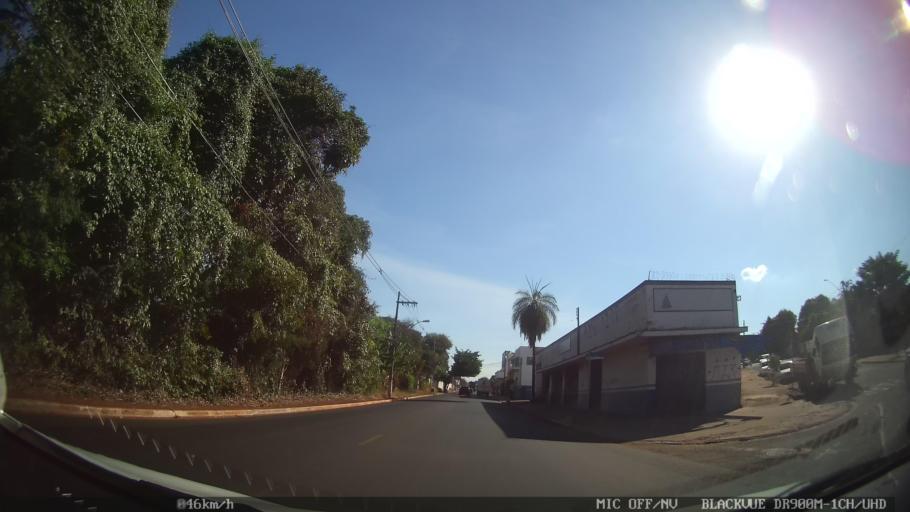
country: BR
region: Sao Paulo
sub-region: Ribeirao Preto
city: Ribeirao Preto
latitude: -21.1840
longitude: -47.7667
